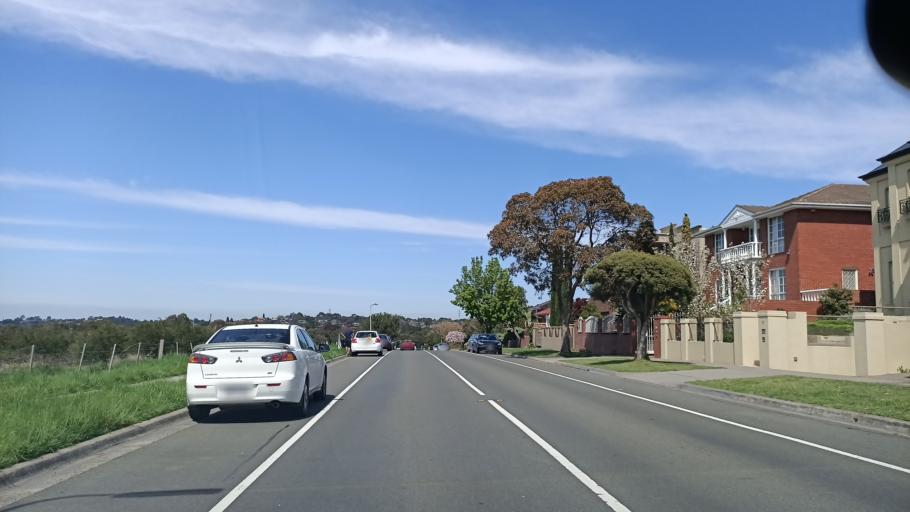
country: AU
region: Victoria
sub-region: Monash
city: Mulgrave
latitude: -37.9168
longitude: 145.2000
